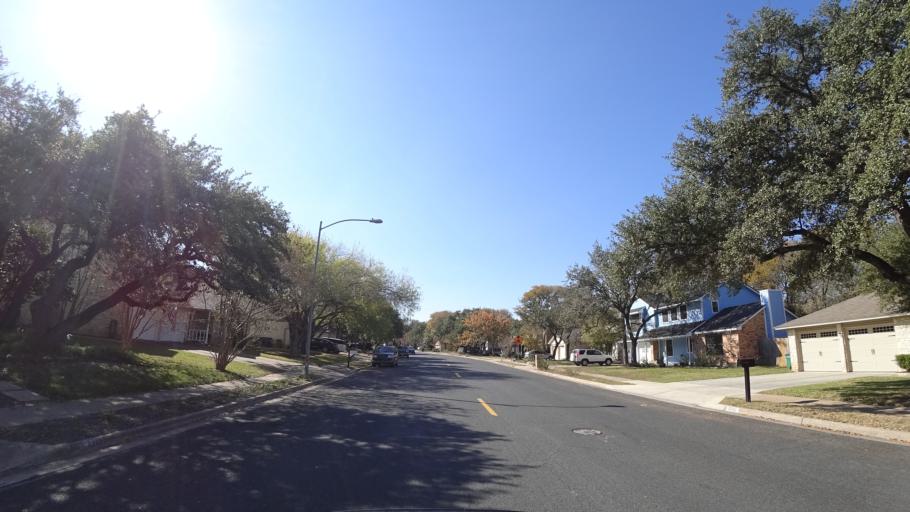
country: US
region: Texas
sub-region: Travis County
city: Shady Hollow
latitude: 30.2243
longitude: -97.8609
